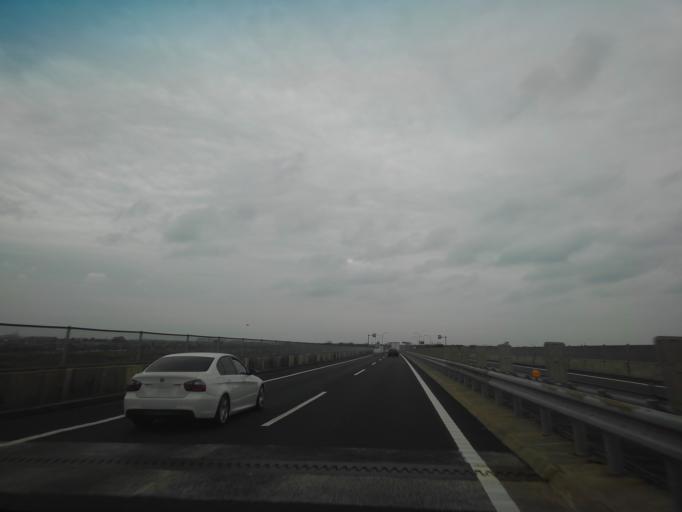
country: JP
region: Chiba
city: Kisarazu
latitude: 35.4142
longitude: 139.9533
